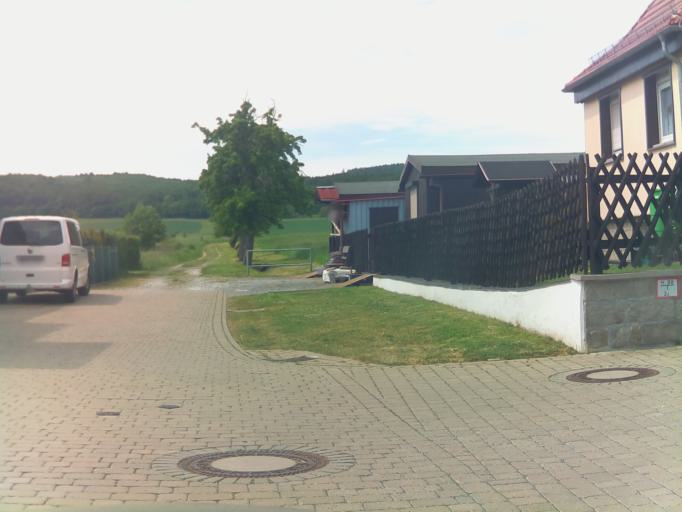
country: DE
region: Saxony-Anhalt
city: Blankenburg
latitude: 51.7724
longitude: 10.9649
